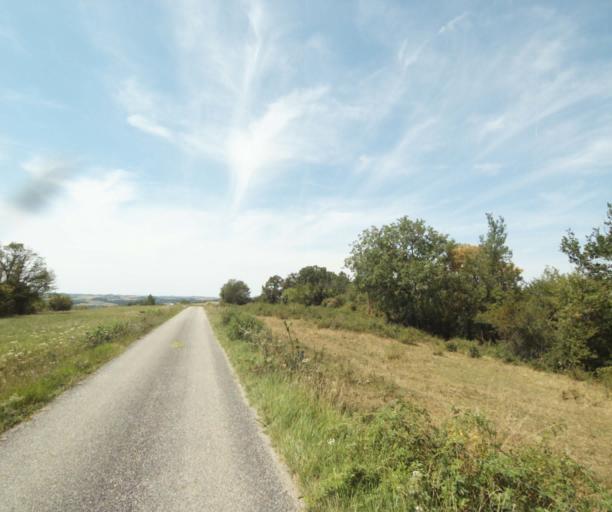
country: FR
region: Midi-Pyrenees
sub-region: Departement de la Haute-Garonne
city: Gaillac-Toulza
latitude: 43.2241
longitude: 1.4136
